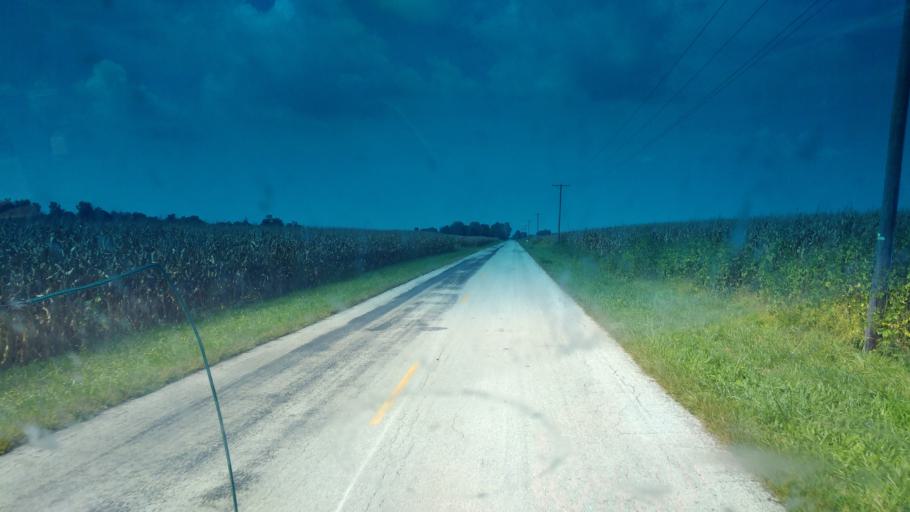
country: US
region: Ohio
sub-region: Union County
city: Richwood
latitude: 40.6002
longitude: -83.3466
